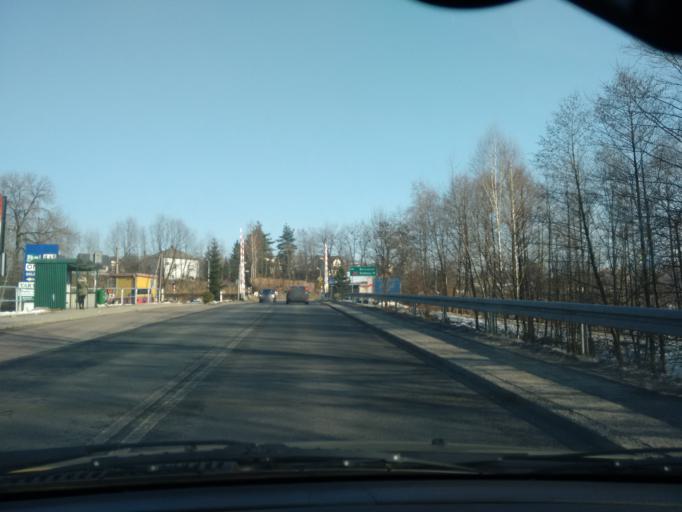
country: PL
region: Lesser Poland Voivodeship
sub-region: Powiat oswiecimski
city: Bulowice
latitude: 49.8755
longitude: 19.2898
